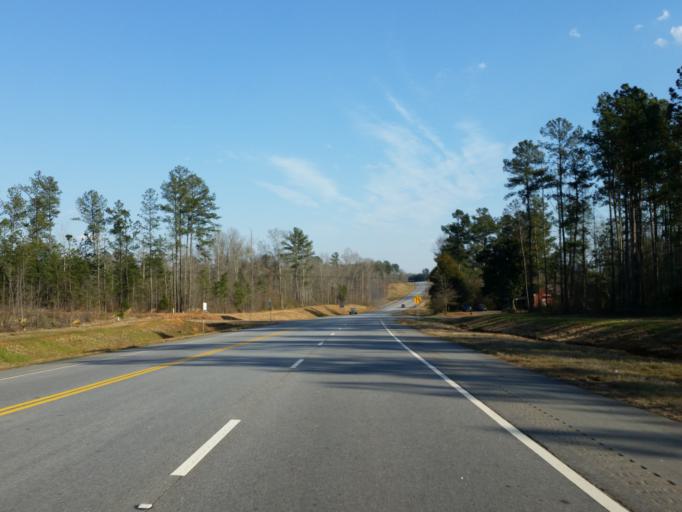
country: US
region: Georgia
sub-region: Monroe County
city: Forsyth
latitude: 33.0352
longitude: -83.9959
